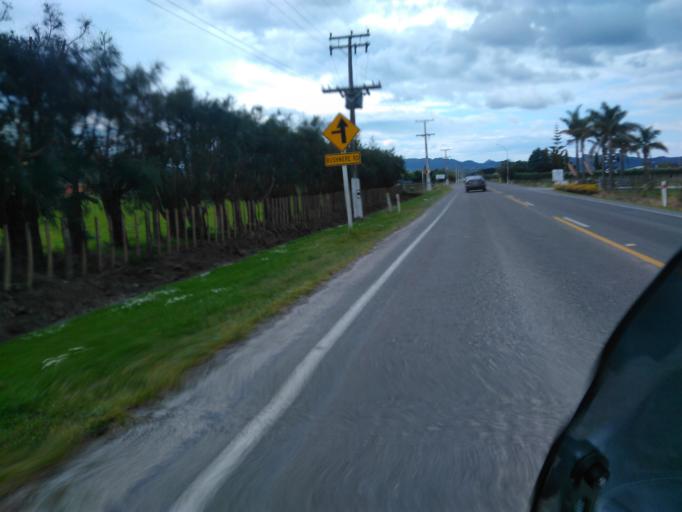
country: NZ
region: Gisborne
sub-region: Gisborne District
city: Gisborne
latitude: -38.6553
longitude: 177.9521
